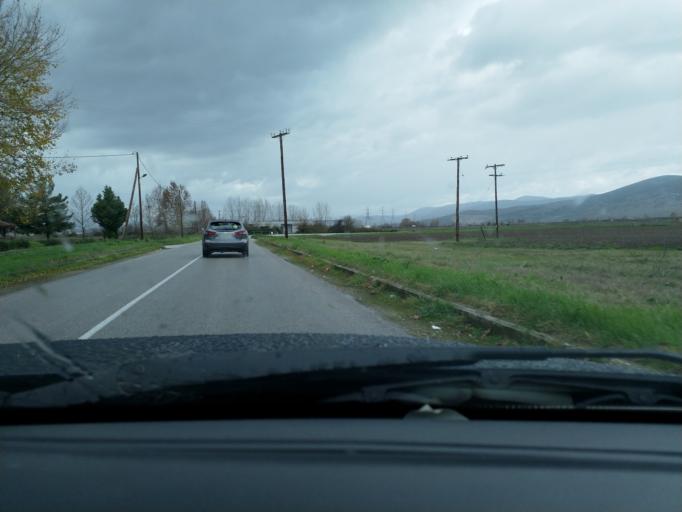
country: GR
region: Thessaly
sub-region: Trikala
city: Taxiarches
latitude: 39.5509
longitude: 21.8907
